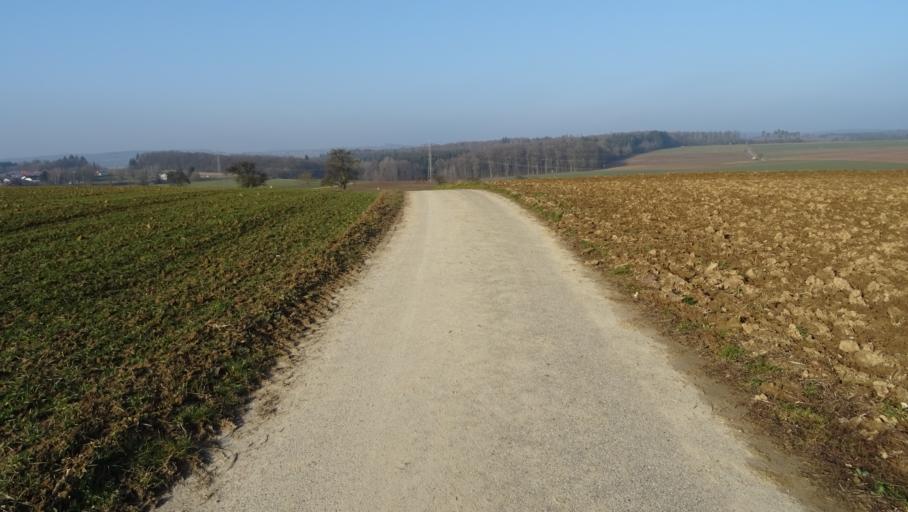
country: DE
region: Baden-Wuerttemberg
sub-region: Karlsruhe Region
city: Neckargerach
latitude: 49.3940
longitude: 9.1089
